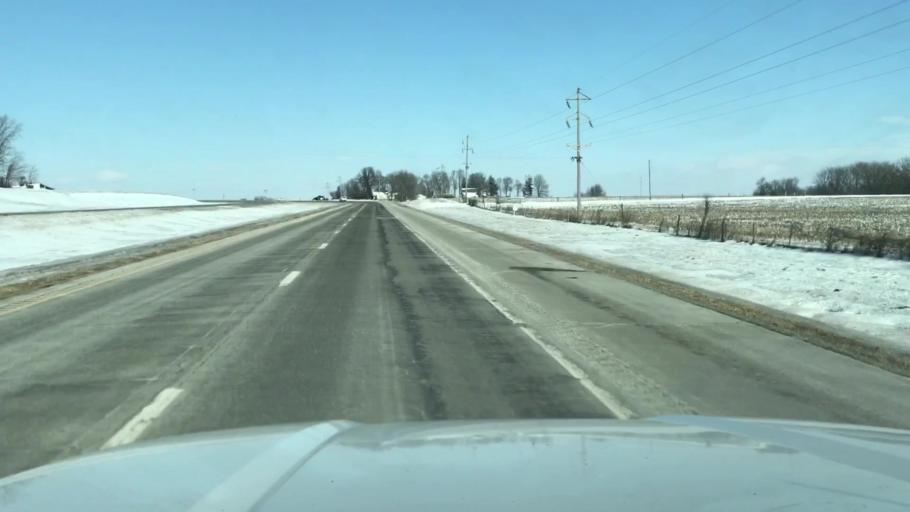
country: US
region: Missouri
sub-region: Nodaway County
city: Maryville
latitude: 40.2678
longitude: -94.8665
